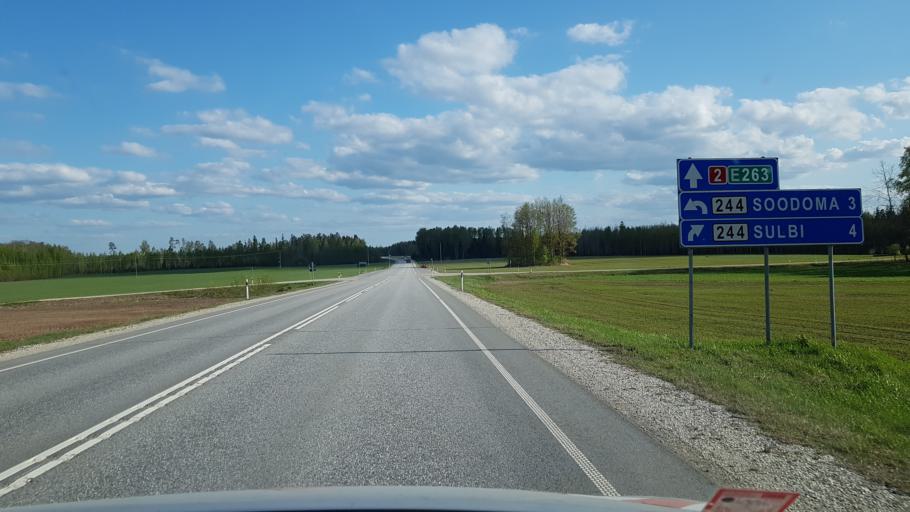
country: EE
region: Vorumaa
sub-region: Voru linn
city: Voru
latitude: 57.9352
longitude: 26.7979
